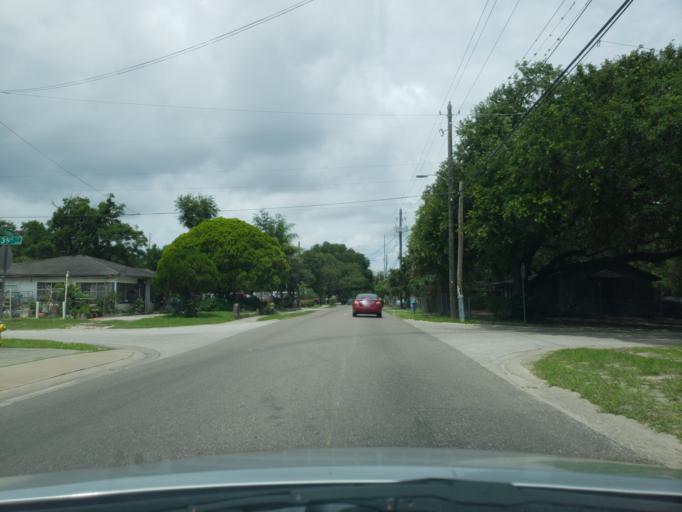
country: US
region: Florida
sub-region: Hillsborough County
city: Temple Terrace
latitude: 28.0034
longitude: -82.4160
